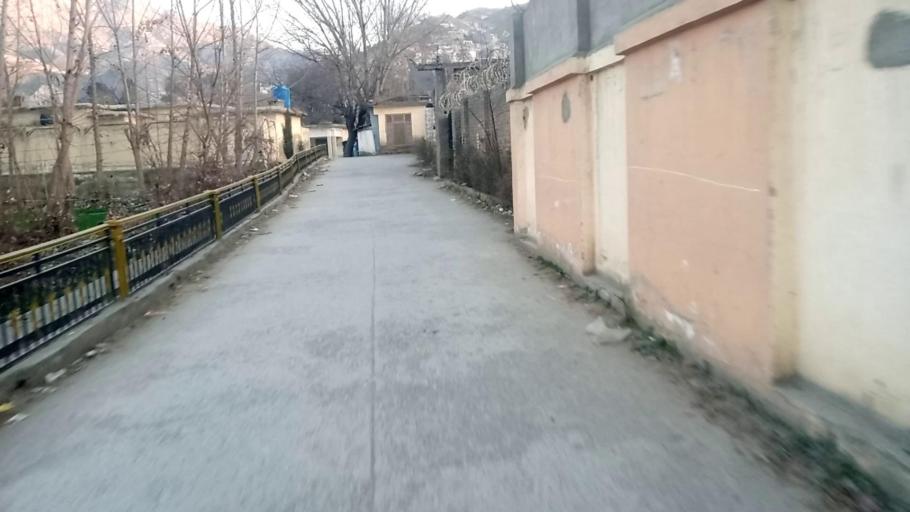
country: PK
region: Khyber Pakhtunkhwa
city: Saidu Sharif
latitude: 34.7469
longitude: 72.3522
